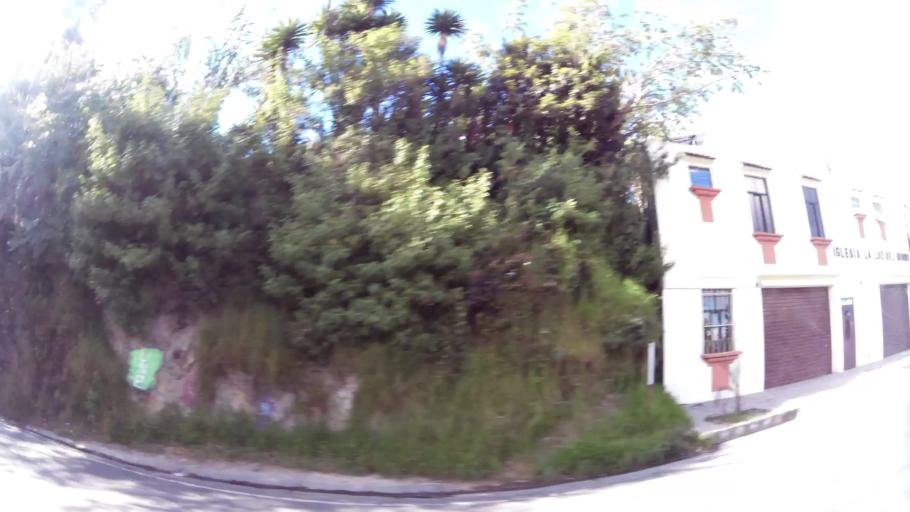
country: GT
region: Quiche
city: Chichicastenango
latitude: 14.9356
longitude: -91.1089
